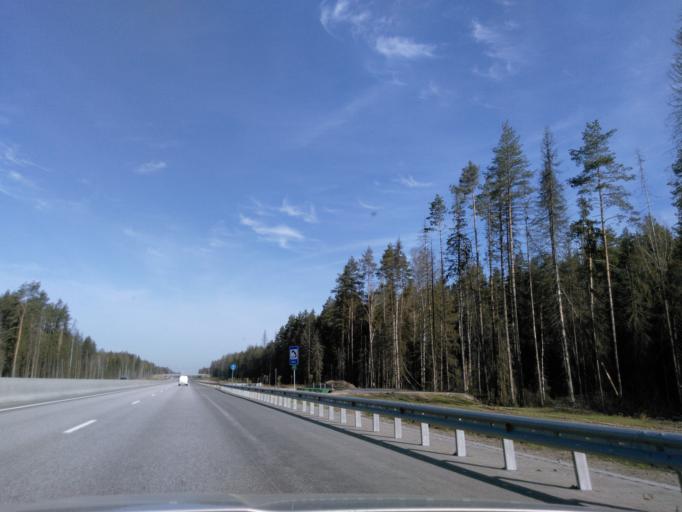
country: RU
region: Moskovskaya
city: Mendeleyevo
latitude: 56.0565
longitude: 37.2499
